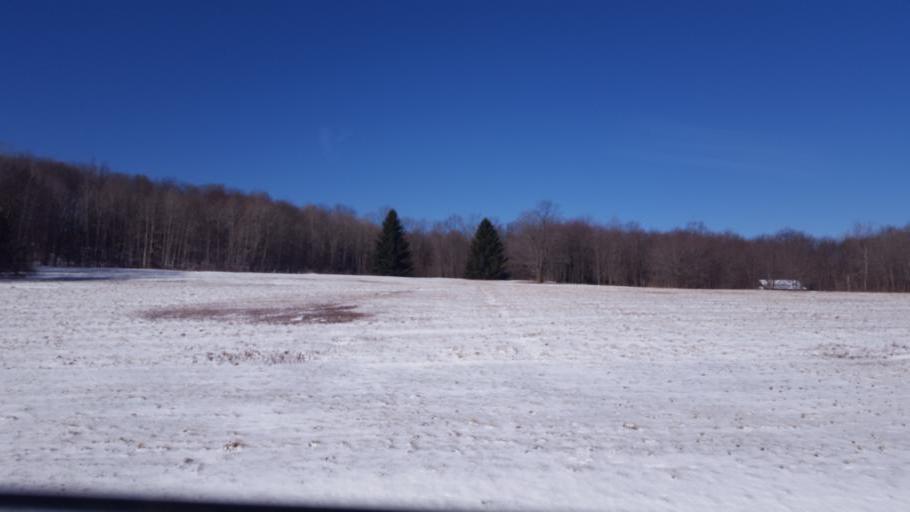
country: US
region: New York
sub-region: Allegany County
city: Wellsville
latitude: 42.1528
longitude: -77.9340
